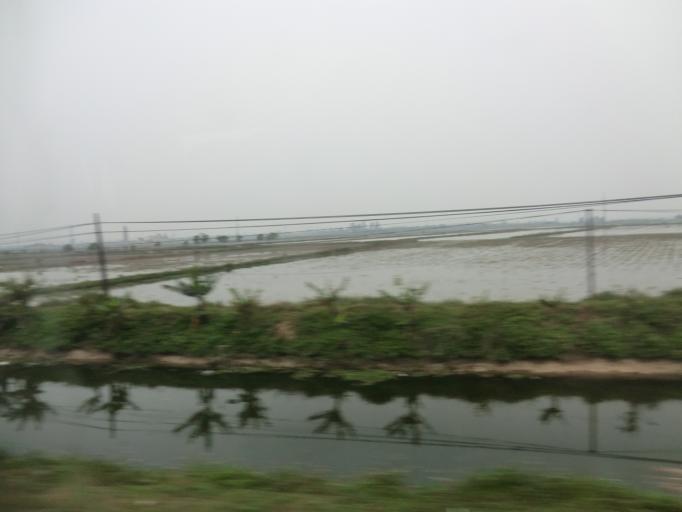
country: VN
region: Nam Dinh
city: Thi Tran Lam
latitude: 20.2928
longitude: 106.0219
